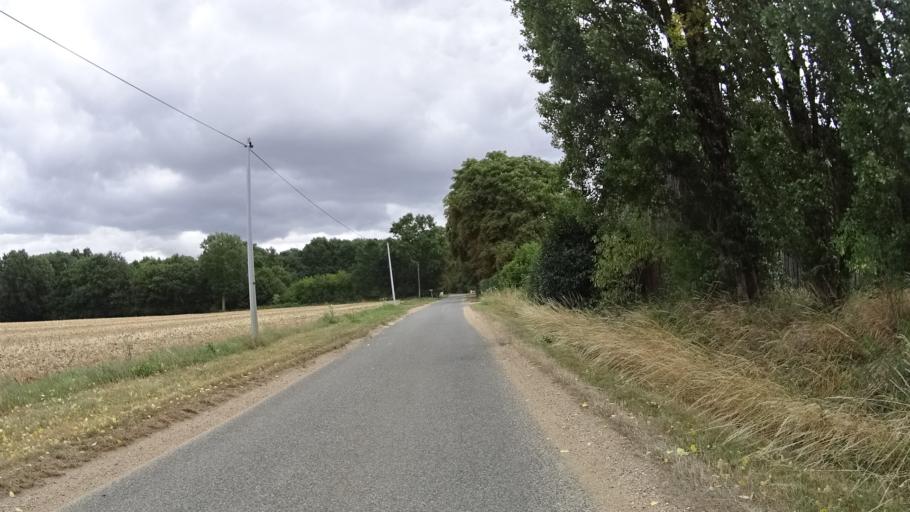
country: FR
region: Centre
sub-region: Departement du Loiret
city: Amilly
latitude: 47.9478
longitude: 2.8034
